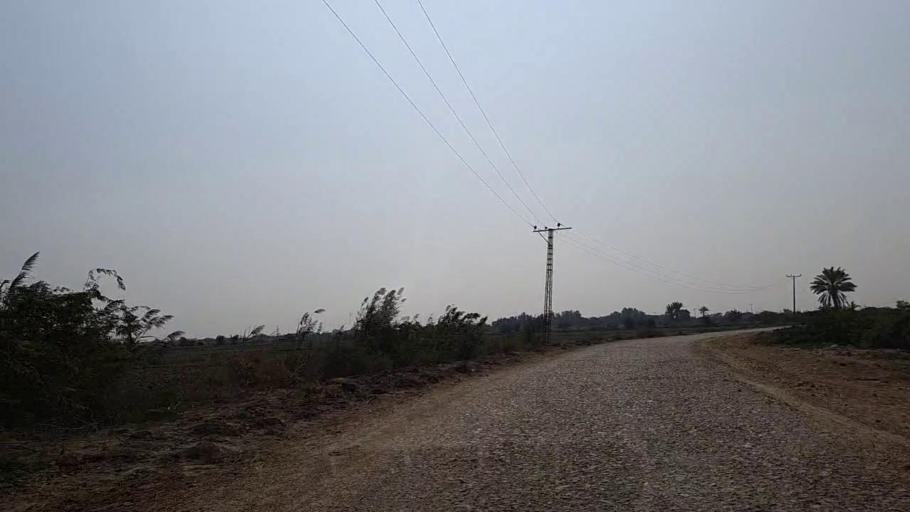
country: PK
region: Sindh
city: Thatta
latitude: 24.7368
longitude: 67.7703
